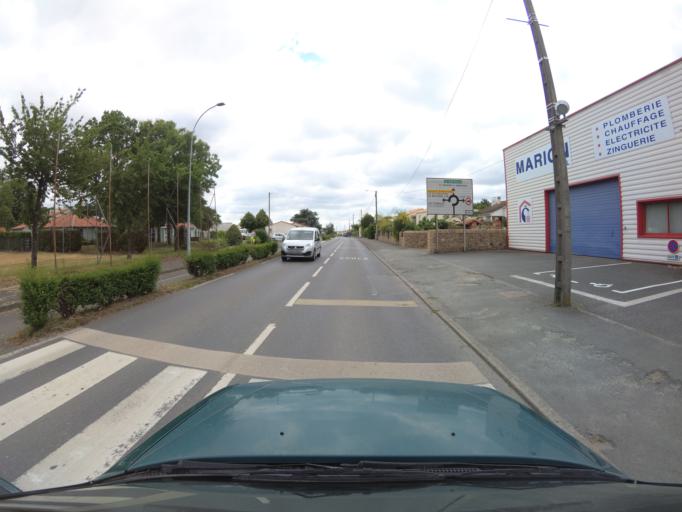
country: FR
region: Pays de la Loire
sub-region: Departement de la Vendee
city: Montaigu
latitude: 46.9719
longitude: -1.3065
